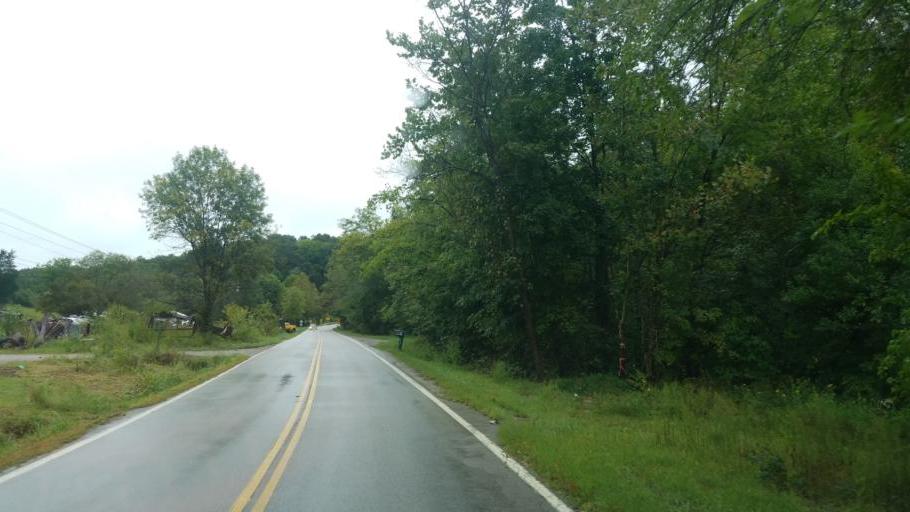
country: US
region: Ohio
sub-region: Adams County
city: West Union
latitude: 38.7667
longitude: -83.5266
